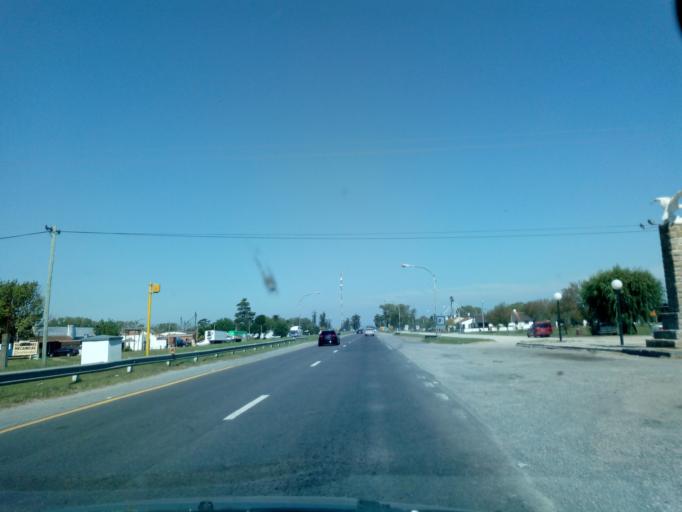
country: AR
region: Buenos Aires
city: Coronel Vidal
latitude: -37.2739
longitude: -57.7667
